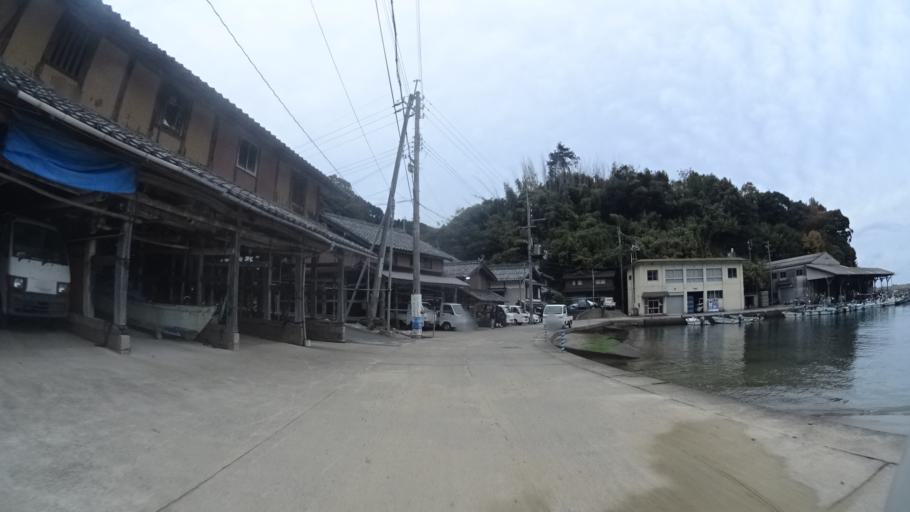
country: JP
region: Kyoto
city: Maizuru
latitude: 35.5788
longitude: 135.4479
